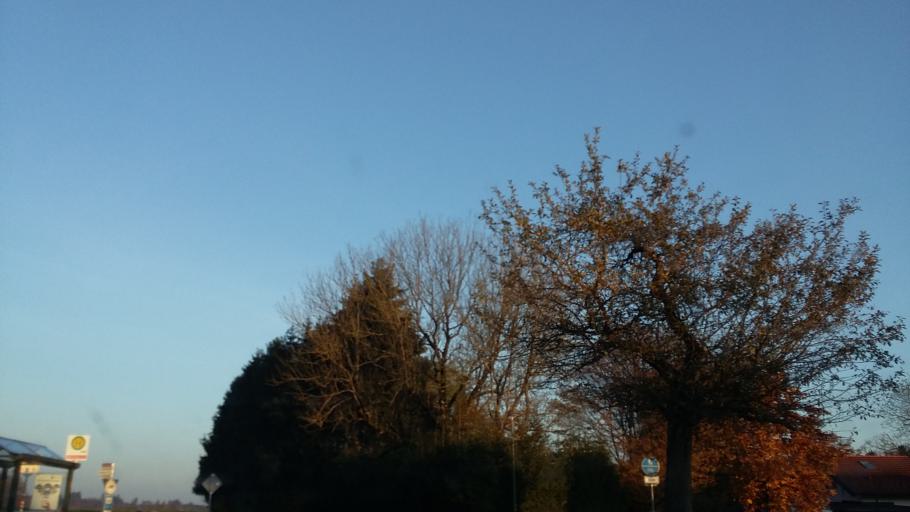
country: DE
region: Bavaria
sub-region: Upper Bavaria
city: Gstadt am Chiemsee
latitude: 47.8911
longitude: 12.3874
